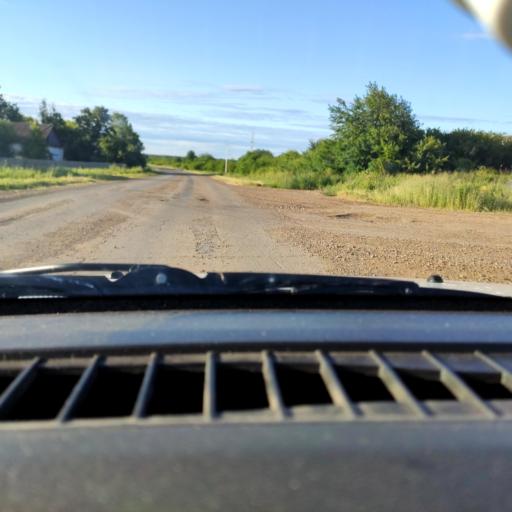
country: RU
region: Perm
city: Uinskoye
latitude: 57.1070
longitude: 56.5328
